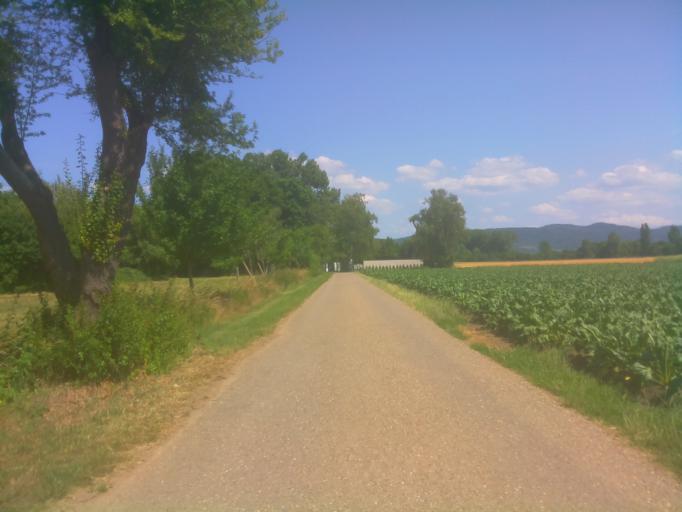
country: DE
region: Baden-Wuerttemberg
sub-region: Karlsruhe Region
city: Heddesheim
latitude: 49.5214
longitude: 8.6087
